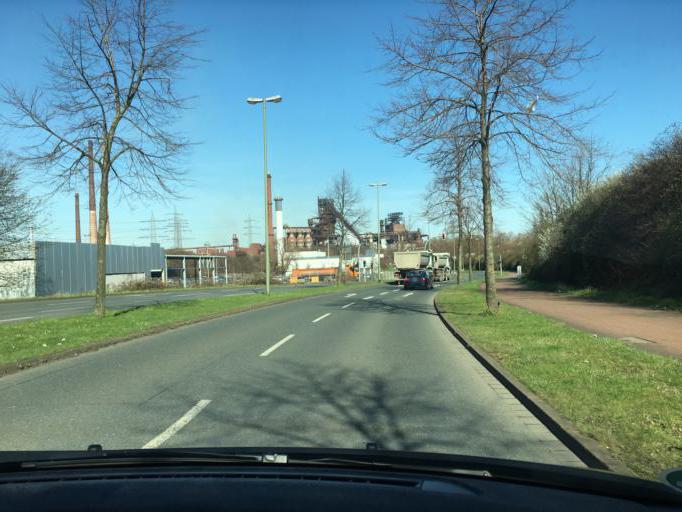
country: DE
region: North Rhine-Westphalia
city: Meiderich
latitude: 51.4988
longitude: 6.7485
